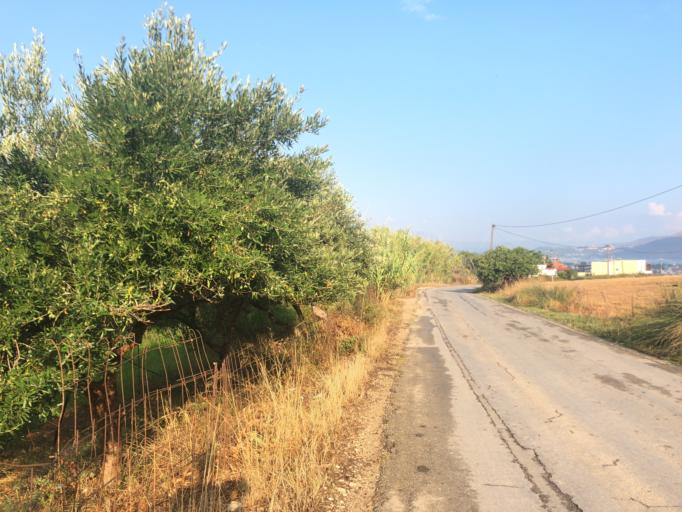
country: GR
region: Crete
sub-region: Nomos Chanias
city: Georgioupolis
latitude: 35.3447
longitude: 24.3091
